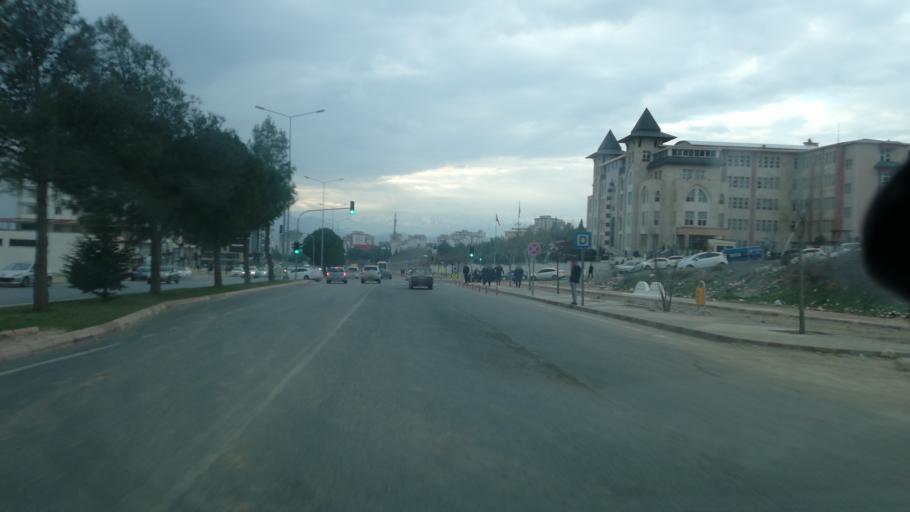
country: TR
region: Kahramanmaras
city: Kahramanmaras
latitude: 37.5994
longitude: 36.8384
